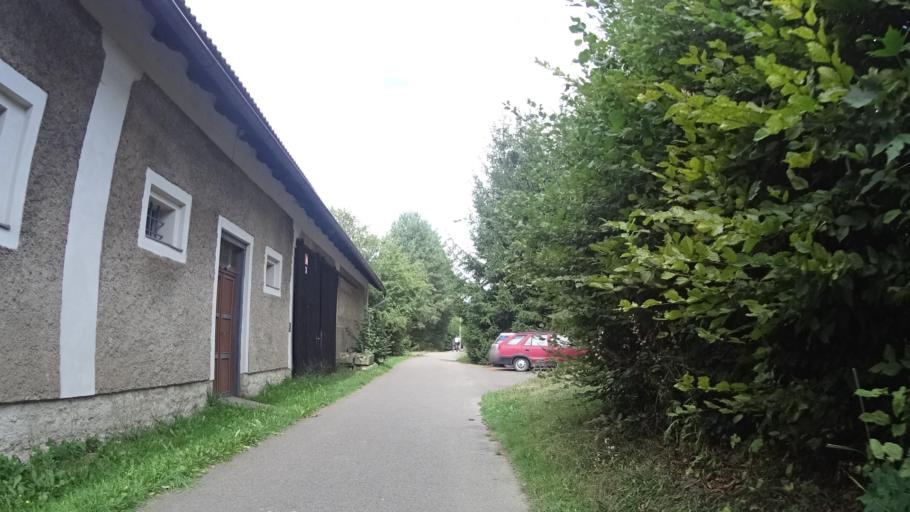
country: CZ
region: Pardubicky
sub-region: Okres Usti nad Orlici
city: Usti nad Orlici
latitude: 49.9857
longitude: 16.4030
